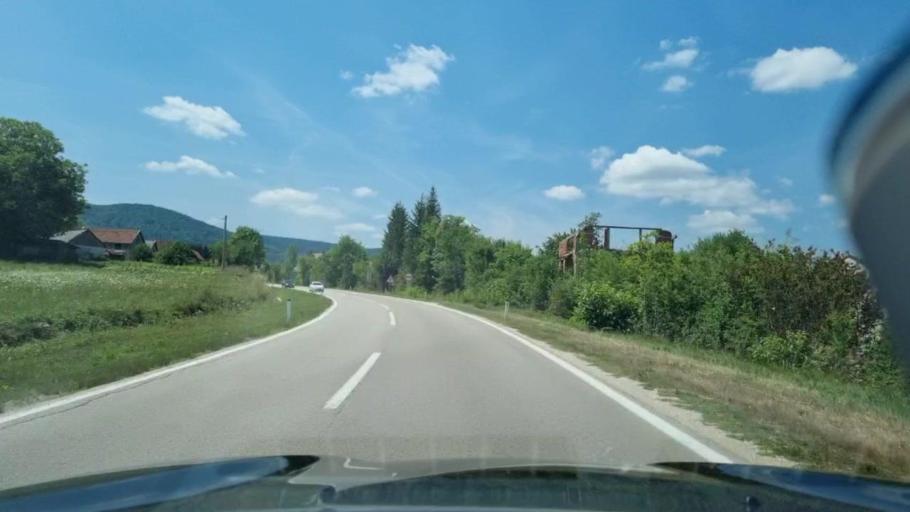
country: BA
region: Federation of Bosnia and Herzegovina
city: Velagici
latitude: 44.5594
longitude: 16.7128
